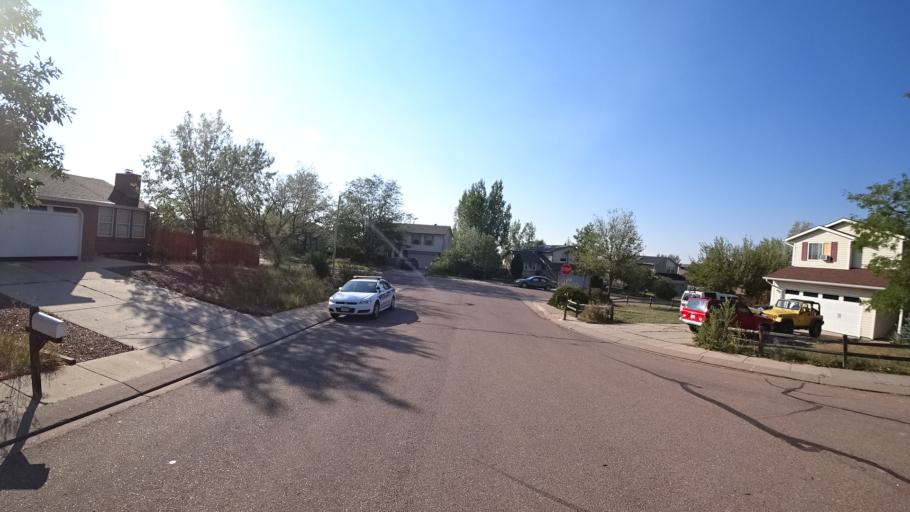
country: US
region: Colorado
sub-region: El Paso County
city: Stratmoor
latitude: 38.7770
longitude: -104.8011
